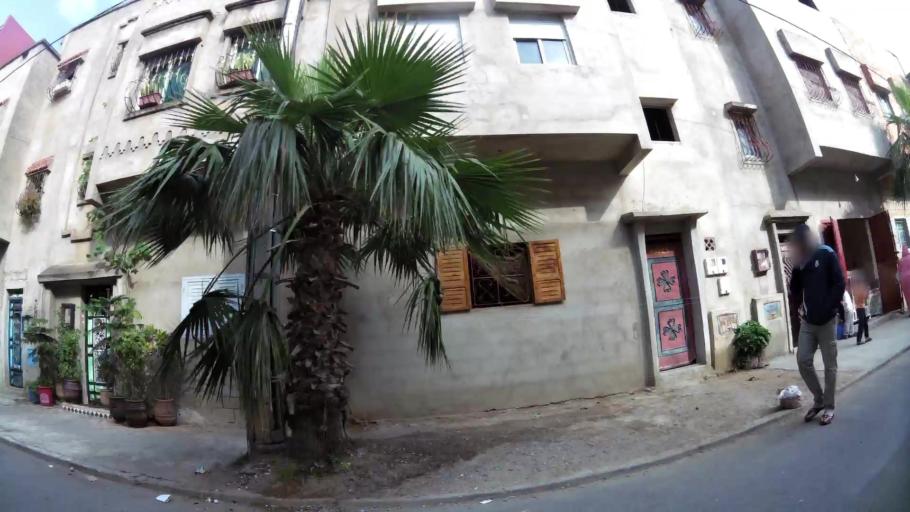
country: MA
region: Rabat-Sale-Zemmour-Zaer
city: Sale
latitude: 34.0573
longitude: -6.7750
